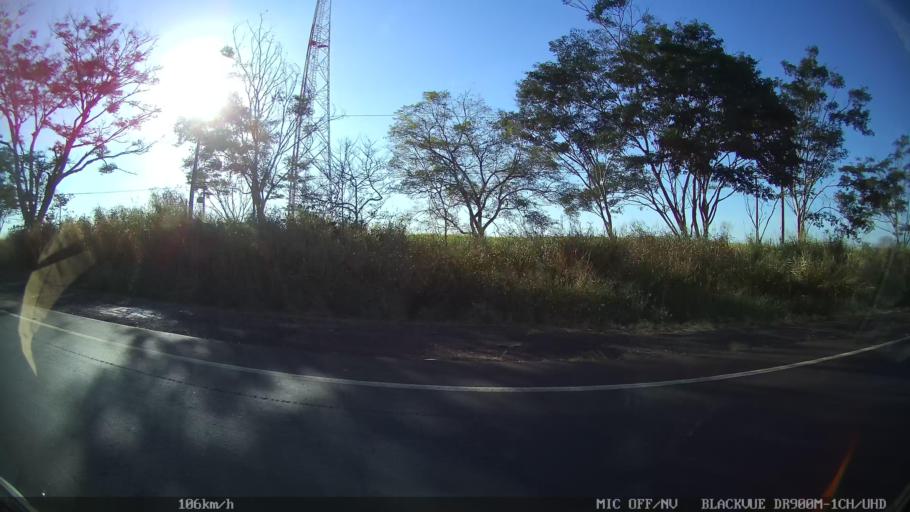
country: BR
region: Sao Paulo
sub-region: Guapiacu
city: Guapiacu
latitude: -20.7352
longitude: -49.0743
